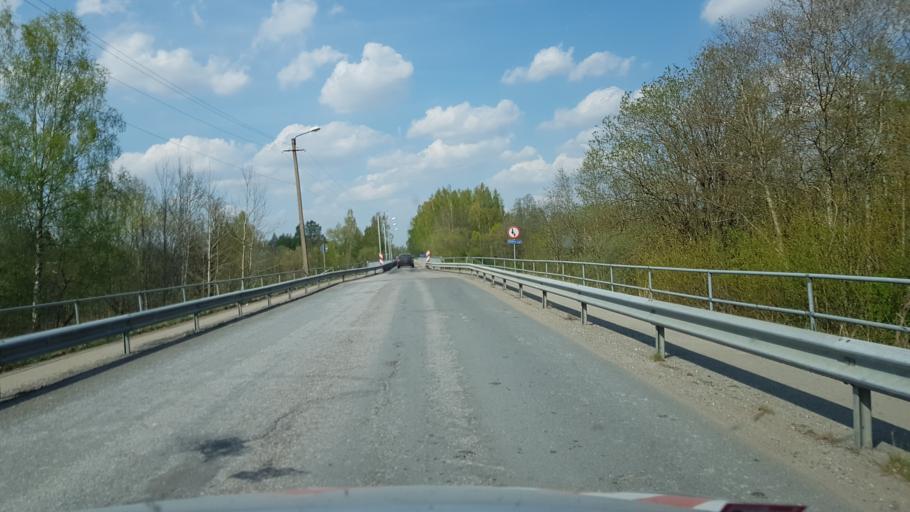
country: EE
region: Paernumaa
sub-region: Sindi linn
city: Sindi
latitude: 58.4160
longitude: 24.6713
